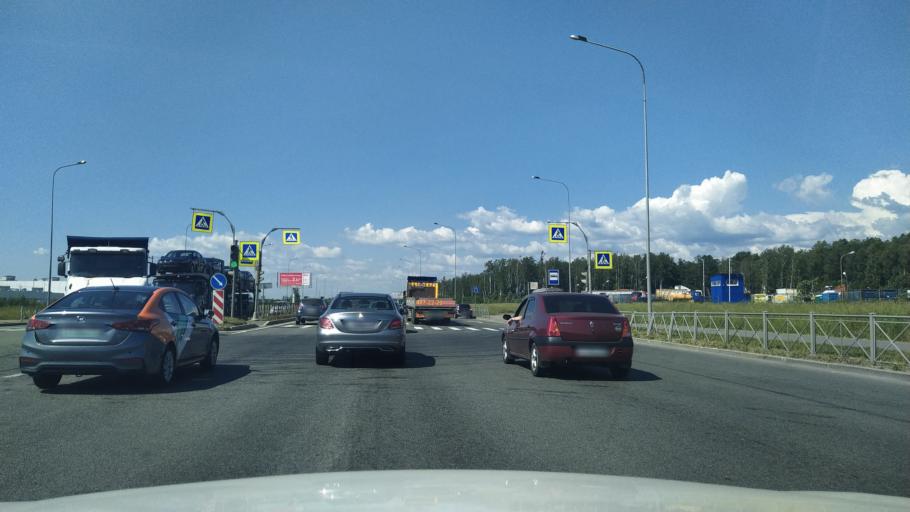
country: RU
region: St.-Petersburg
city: Levashovo
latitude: 60.0645
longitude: 30.1928
